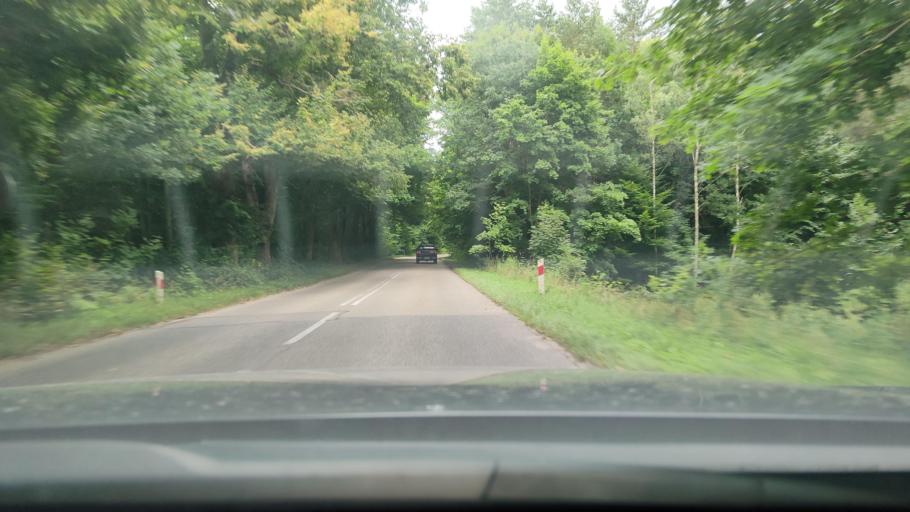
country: PL
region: Pomeranian Voivodeship
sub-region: Powiat pucki
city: Krokowa
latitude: 54.7307
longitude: 18.1683
